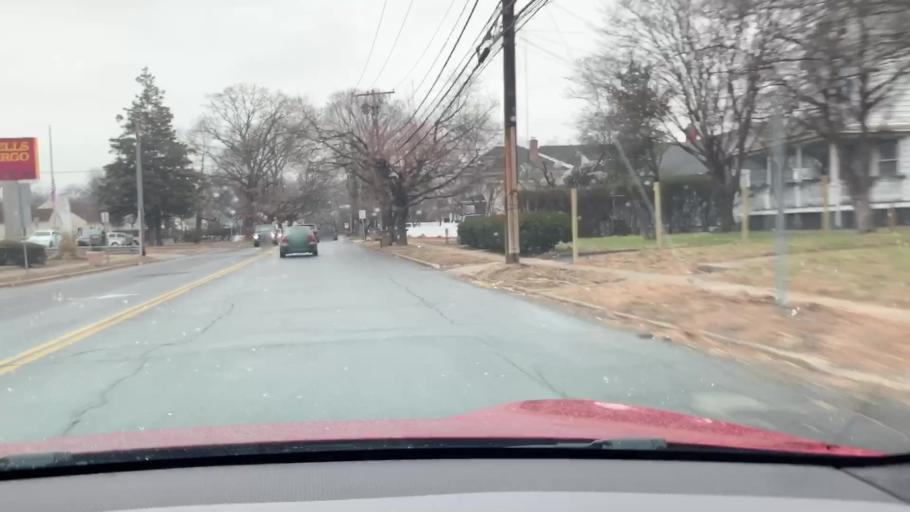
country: US
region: Connecticut
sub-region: Fairfield County
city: Stamford
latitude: 41.0719
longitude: -73.5239
